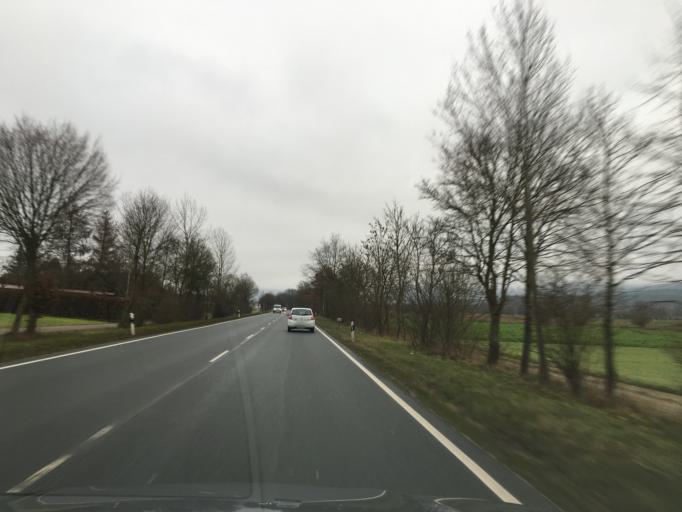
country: DE
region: Bavaria
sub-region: Regierungsbezirk Mittelfranken
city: Henfenfeld
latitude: 49.5120
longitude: 11.3895
